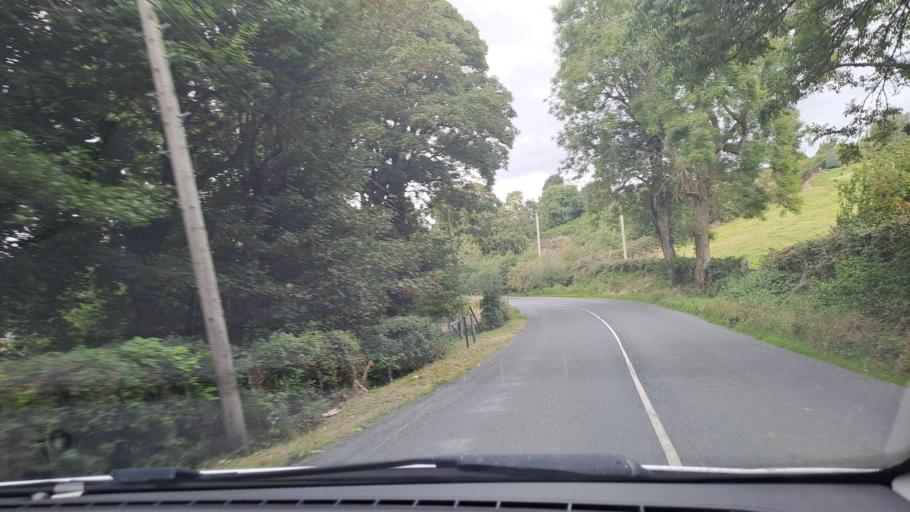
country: IE
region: Ulster
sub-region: An Cabhan
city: Bailieborough
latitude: 54.0034
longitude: -6.9106
